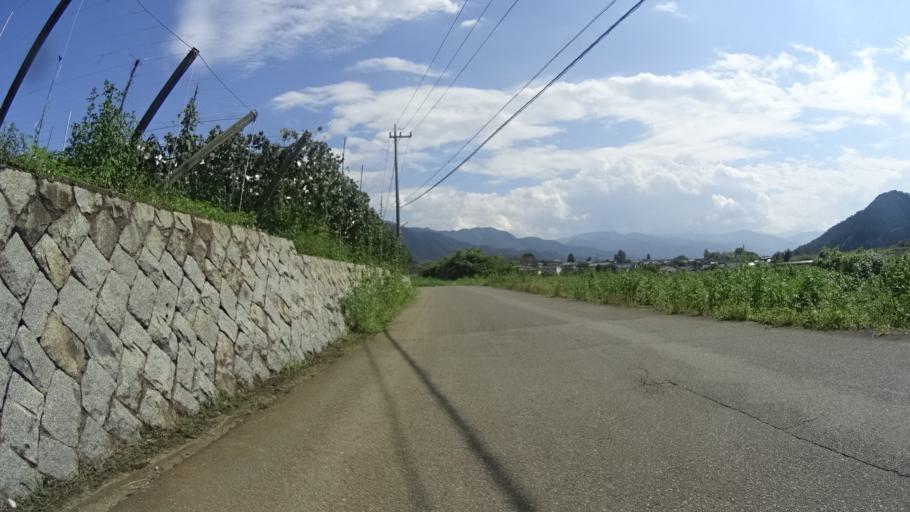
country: JP
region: Yamanashi
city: Enzan
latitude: 35.7210
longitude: 138.7332
